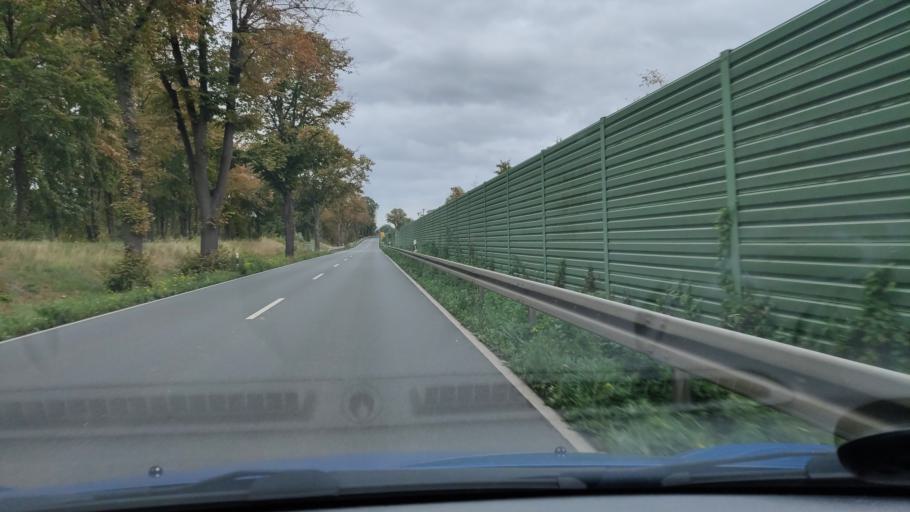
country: DE
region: Lower Saxony
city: Seelze
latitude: 52.3893
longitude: 9.5907
